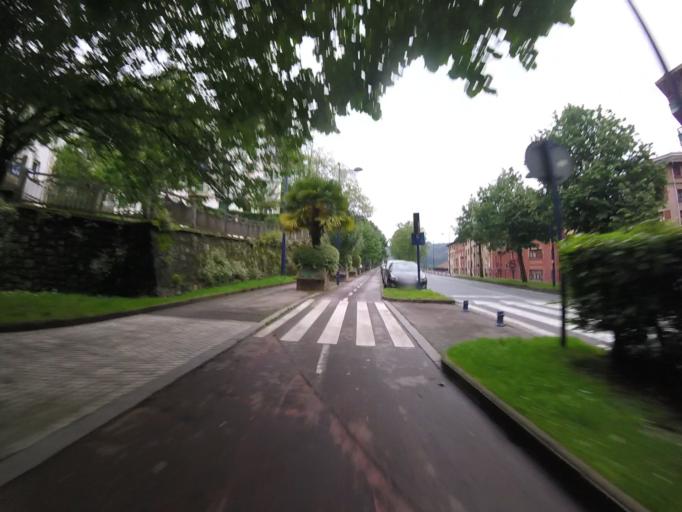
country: ES
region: Basque Country
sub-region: Provincia de Guipuzcoa
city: Errenteria
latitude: 43.3152
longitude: -1.9047
